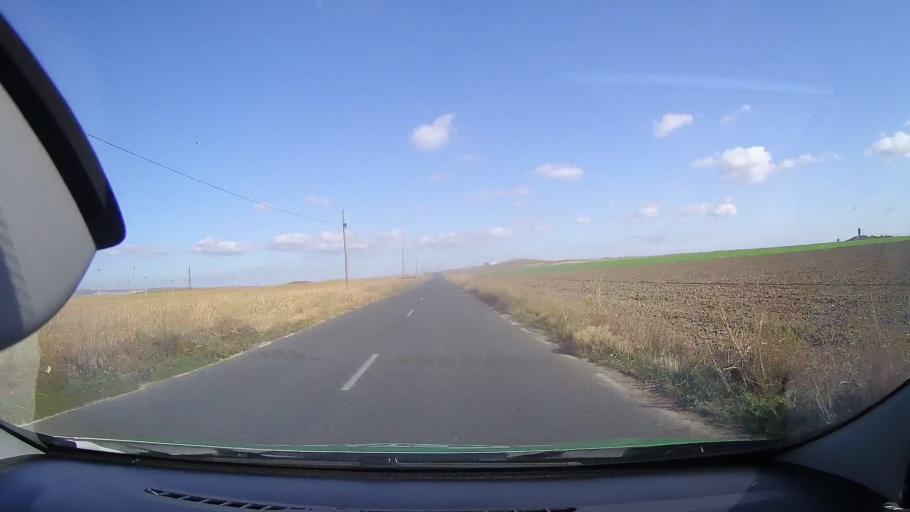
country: RO
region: Tulcea
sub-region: Comuna Ceamurlia de Jos
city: Ceamurlia de Jos
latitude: 44.7387
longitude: 28.6914
